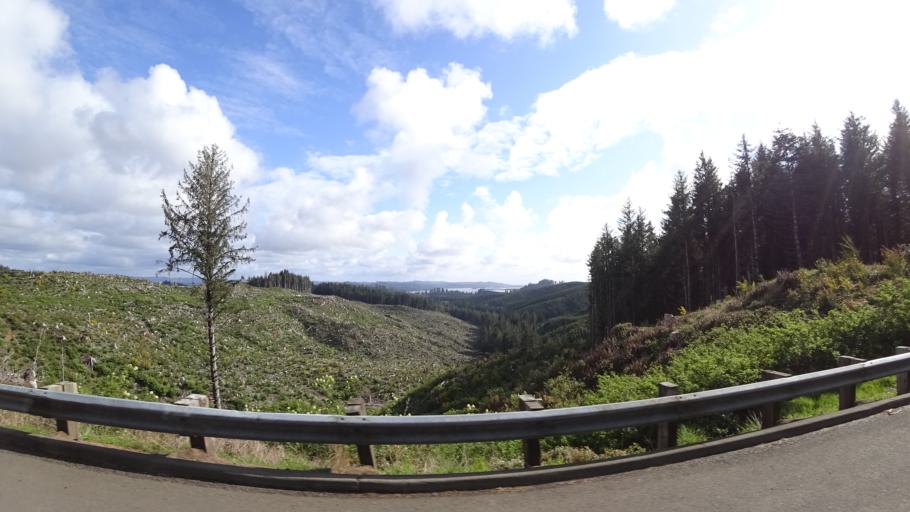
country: US
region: Oregon
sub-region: Douglas County
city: Reedsport
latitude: 43.7706
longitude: -124.1407
